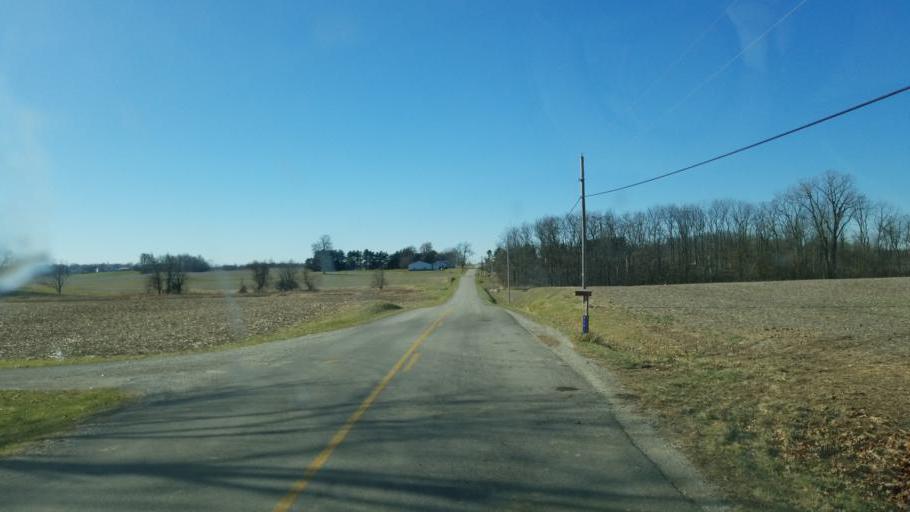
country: US
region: Ohio
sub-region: Crawford County
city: Crestline
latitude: 40.8770
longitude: -82.8229
